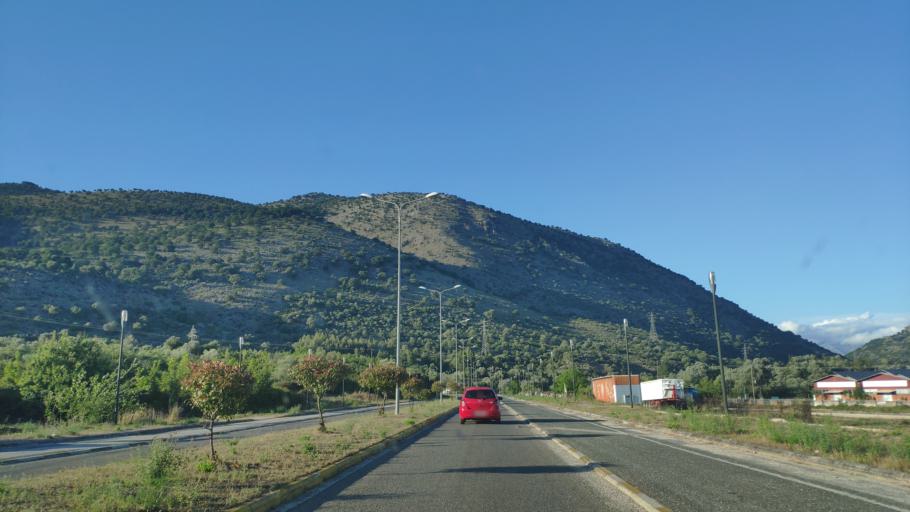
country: GR
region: Epirus
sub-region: Nomos Prevezis
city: Louros
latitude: 39.1719
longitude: 20.7619
